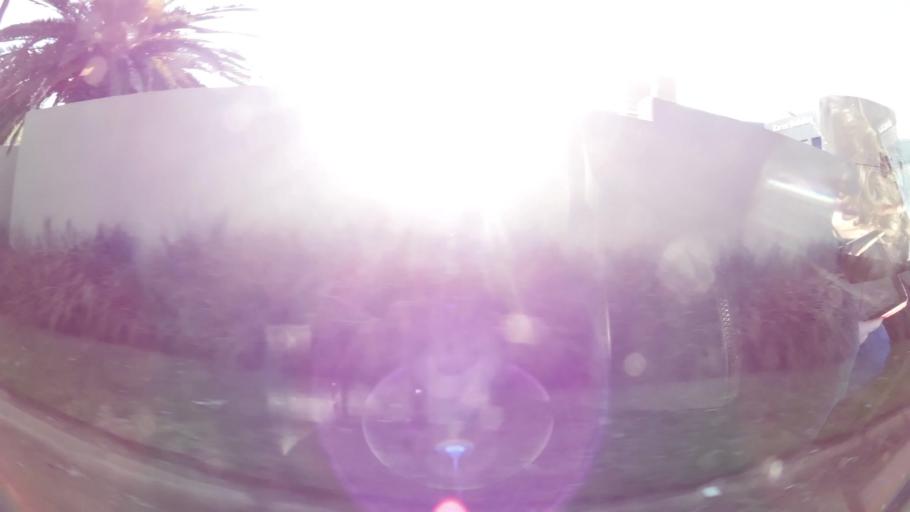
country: ZA
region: Gauteng
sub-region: City of Johannesburg Metropolitan Municipality
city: Modderfontein
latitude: -26.1558
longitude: 28.1757
